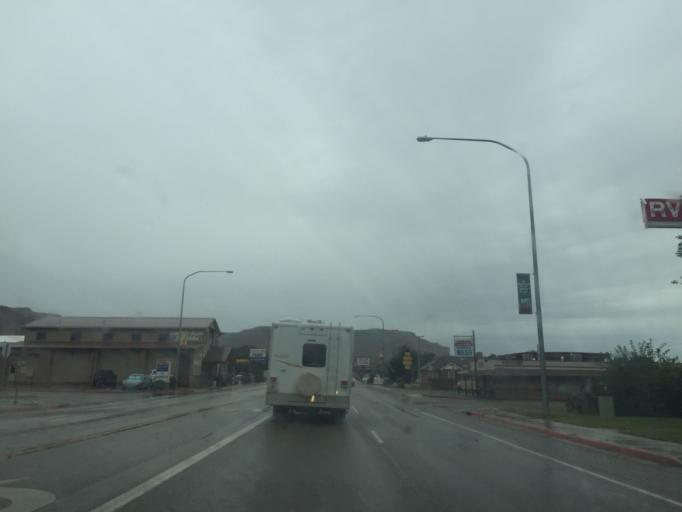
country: US
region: Utah
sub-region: Kane County
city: Kanab
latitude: 37.0429
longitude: -112.5247
